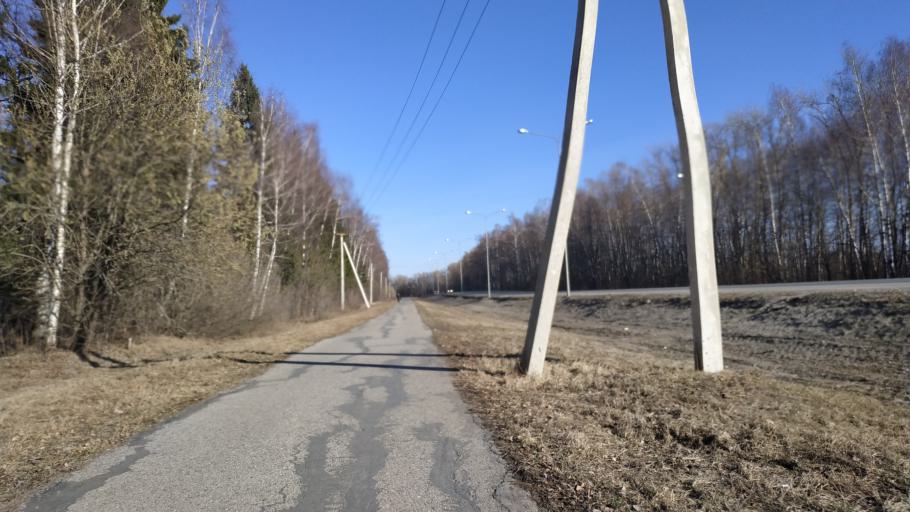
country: RU
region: Chuvashia
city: Novyye Lapsary
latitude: 56.1312
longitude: 47.1132
